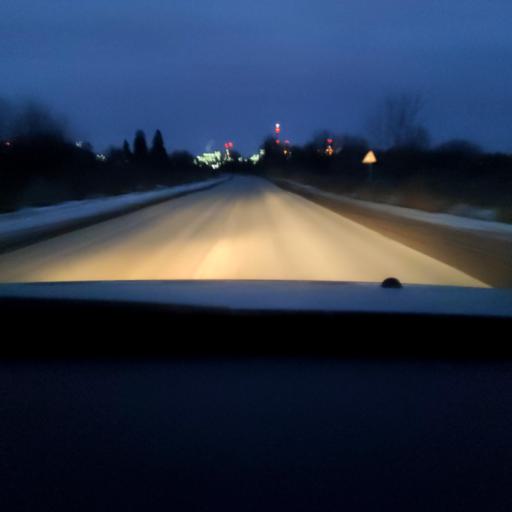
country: RU
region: Perm
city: Gamovo
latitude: 57.8961
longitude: 56.1177
